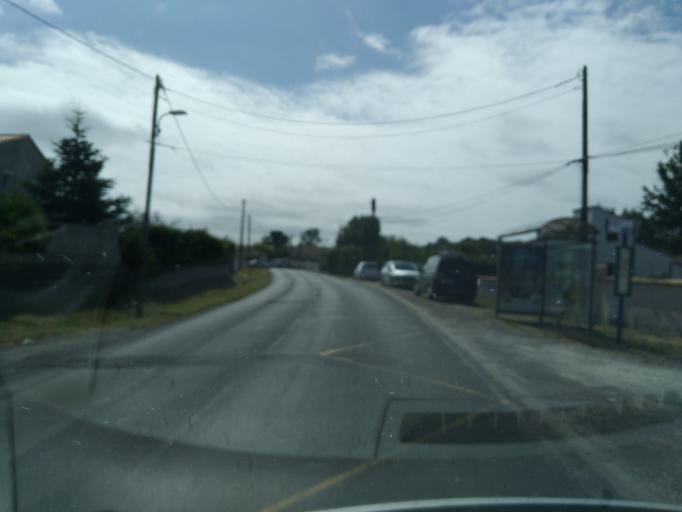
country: FR
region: Poitou-Charentes
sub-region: Departement de la Charente-Maritime
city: Saint-Palais-sur-Mer
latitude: 45.6723
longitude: -1.0861
